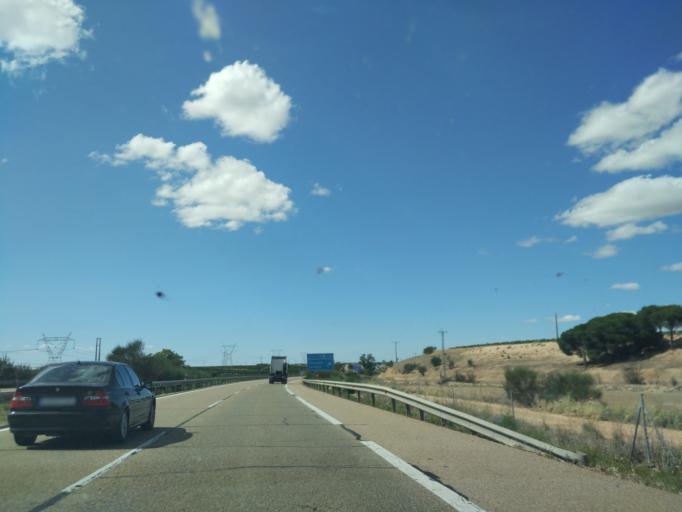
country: ES
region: Castille and Leon
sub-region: Provincia de Valladolid
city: Rueda
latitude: 41.4308
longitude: -4.9708
